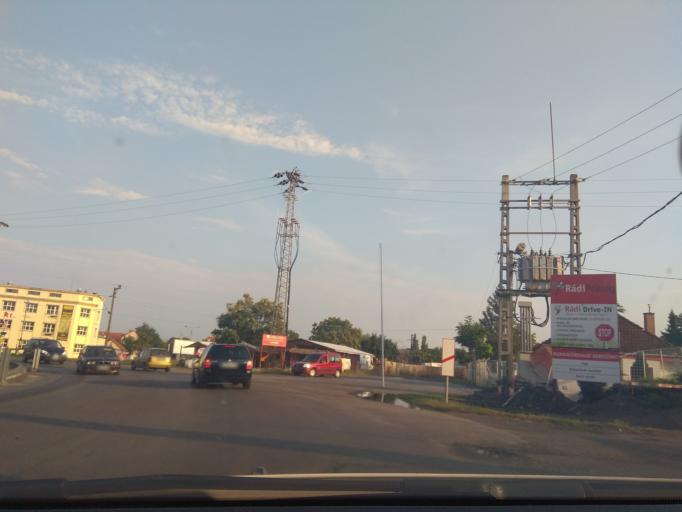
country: HU
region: Heves
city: Eger
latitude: 47.8872
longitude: 20.3970
